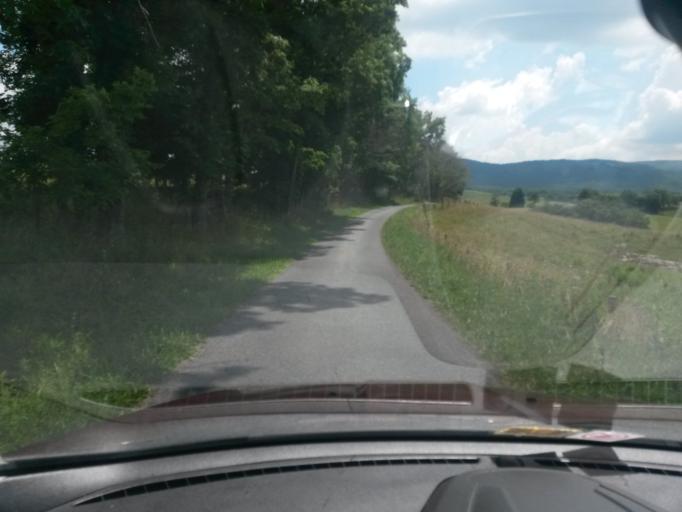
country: US
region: West Virginia
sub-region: Monroe County
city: Union
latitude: 37.5647
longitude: -80.4954
